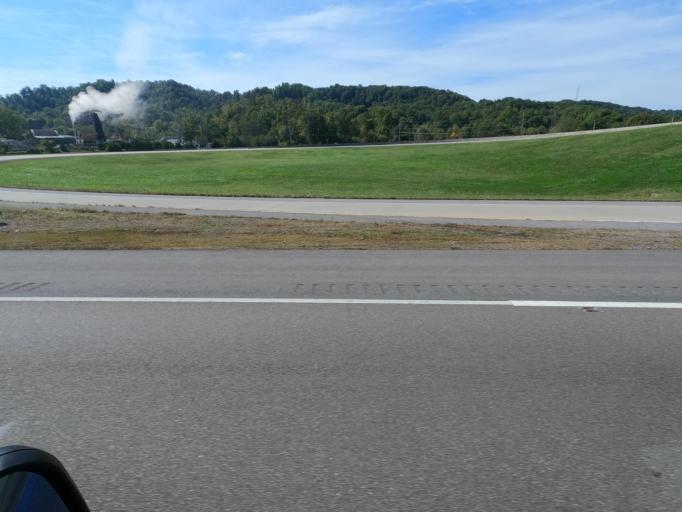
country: US
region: Tennessee
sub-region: Grainger County
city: Bean Station
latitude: 36.3357
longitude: -83.2868
